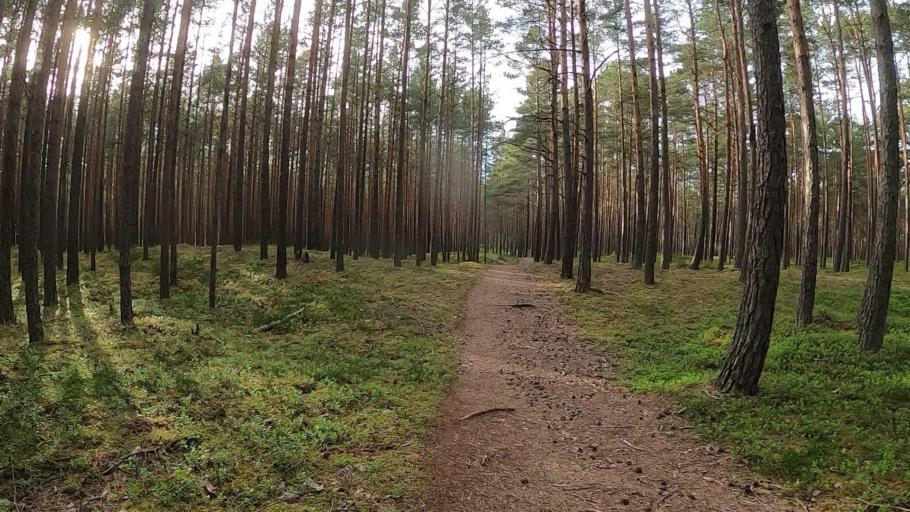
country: LV
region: Riga
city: Jaunciems
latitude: 57.0861
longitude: 24.1440
